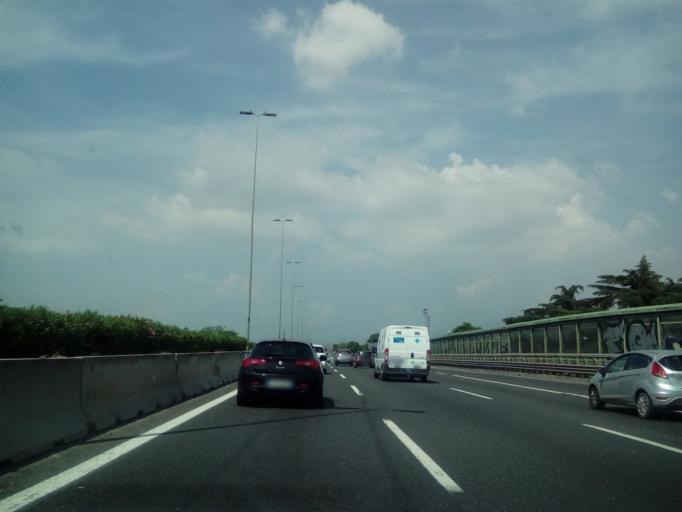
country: IT
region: Latium
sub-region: Citta metropolitana di Roma Capitale
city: Ciampino
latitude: 41.8654
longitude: 12.6016
